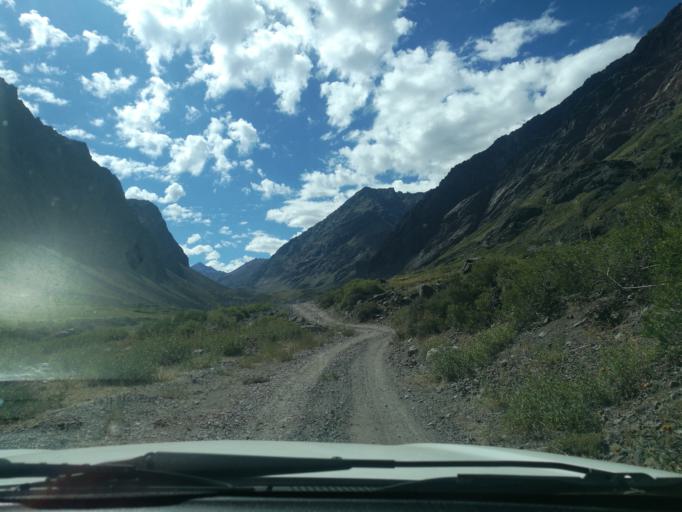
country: CL
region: O'Higgins
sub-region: Provincia de Cachapoal
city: Machali
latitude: -34.3988
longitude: -70.2620
